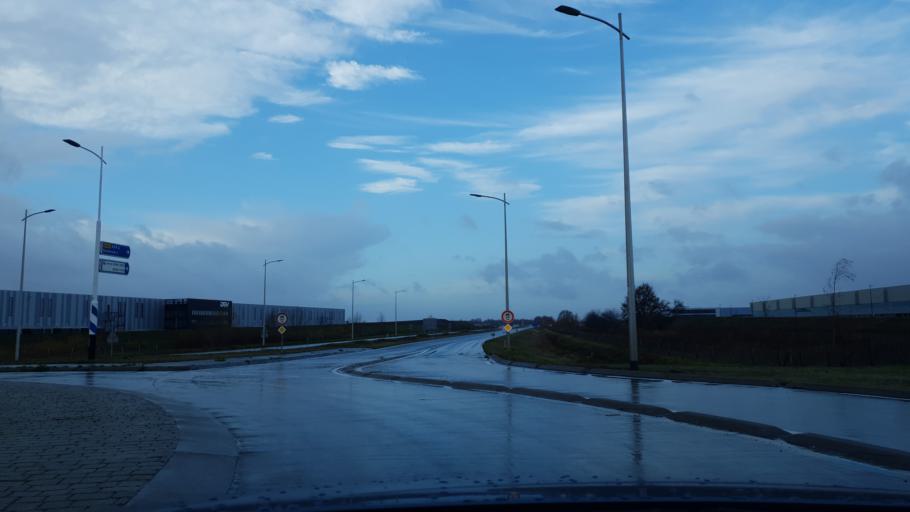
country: NL
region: Limburg
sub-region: Gemeente Peel en Maas
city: Maasbree
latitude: 51.4132
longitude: 6.0958
